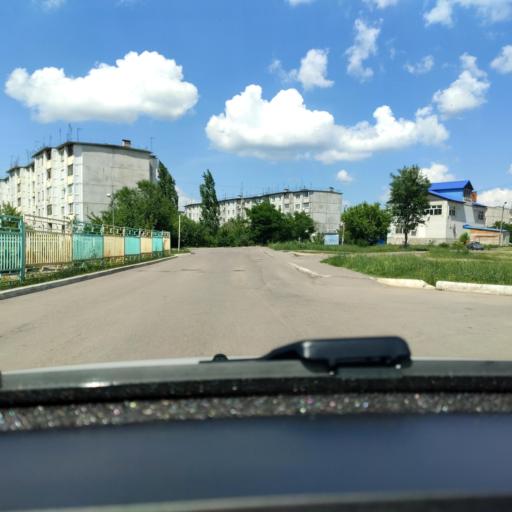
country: RU
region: Voronezj
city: Semiluki
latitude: 51.6925
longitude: 39.0078
